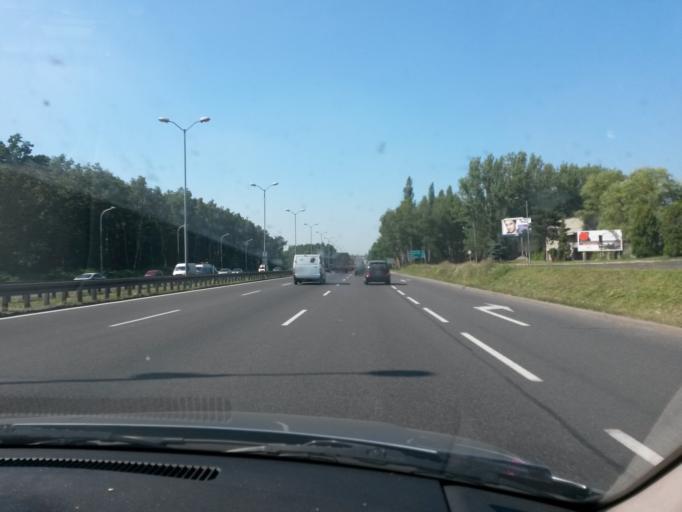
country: PL
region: Silesian Voivodeship
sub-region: Katowice
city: Katowice
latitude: 50.2464
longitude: 19.0506
